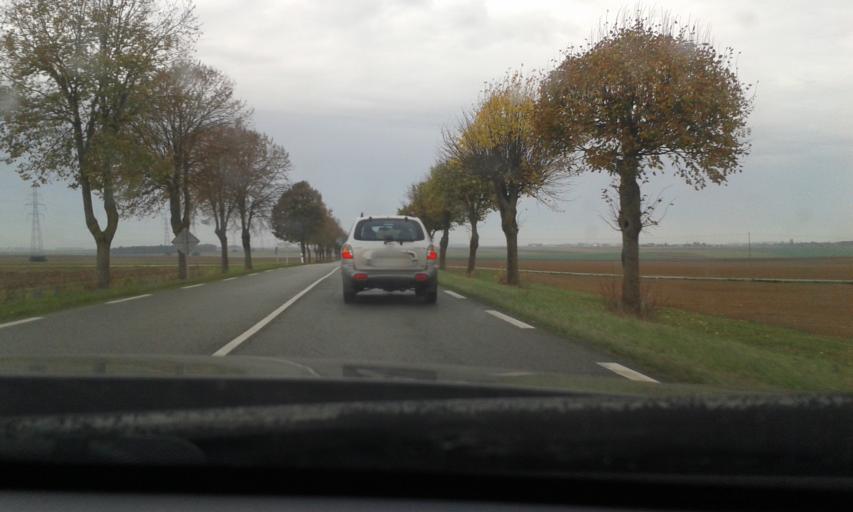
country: FR
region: Centre
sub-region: Departement d'Eure-et-Loir
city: Baigneaux
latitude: 48.1509
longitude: 1.8446
